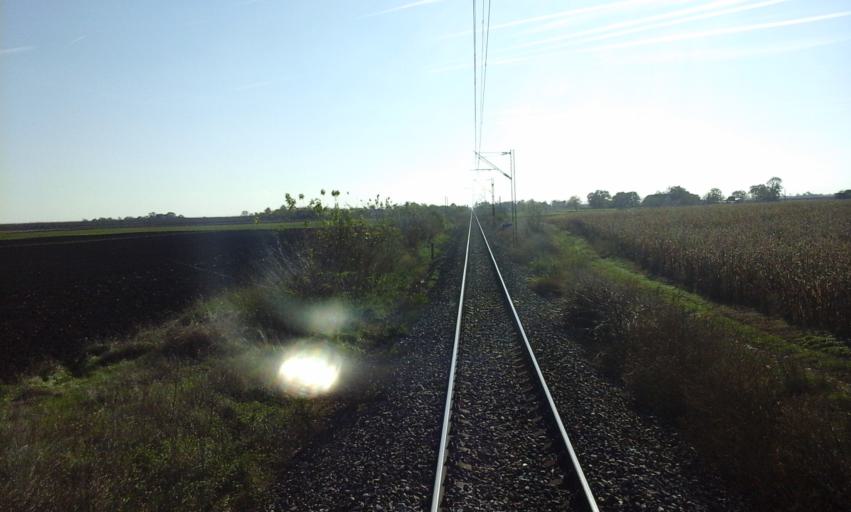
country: RS
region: Autonomna Pokrajina Vojvodina
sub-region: Severnobacki Okrug
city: Subotica
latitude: 45.9935
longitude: 19.6766
